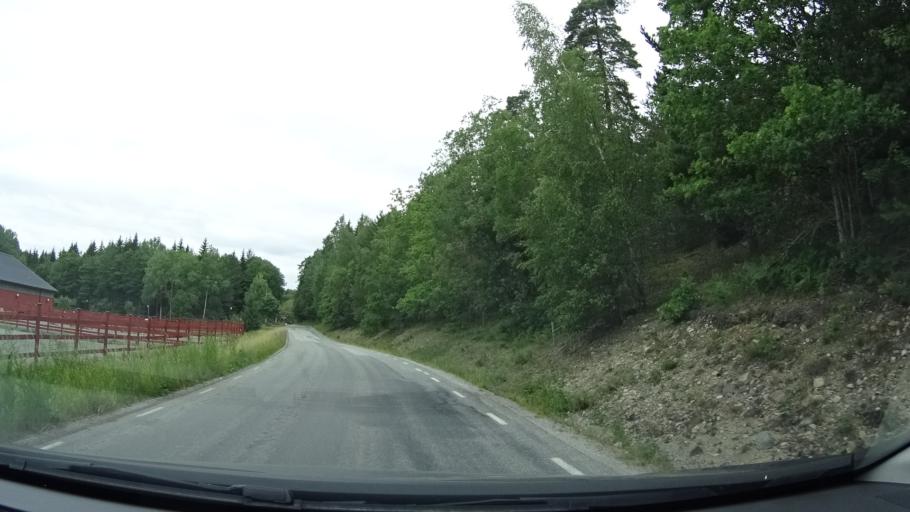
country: SE
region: Stockholm
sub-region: Varmdo Kommun
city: Hemmesta
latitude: 59.3615
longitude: 18.4807
